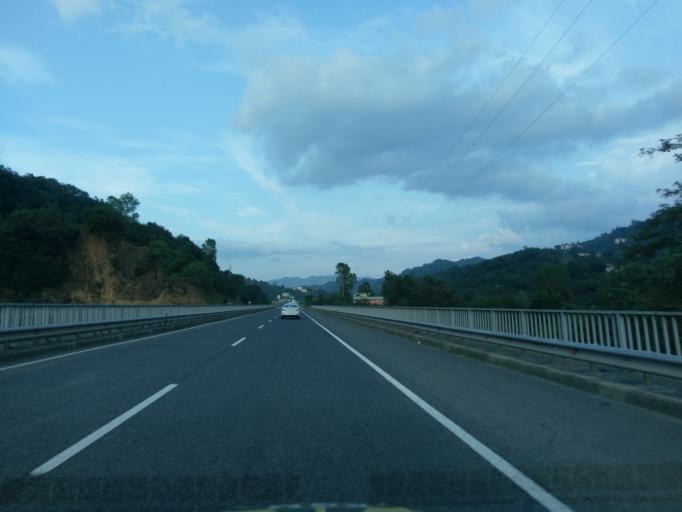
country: TR
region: Ordu
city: Persembe
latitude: 40.9776
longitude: 37.7356
